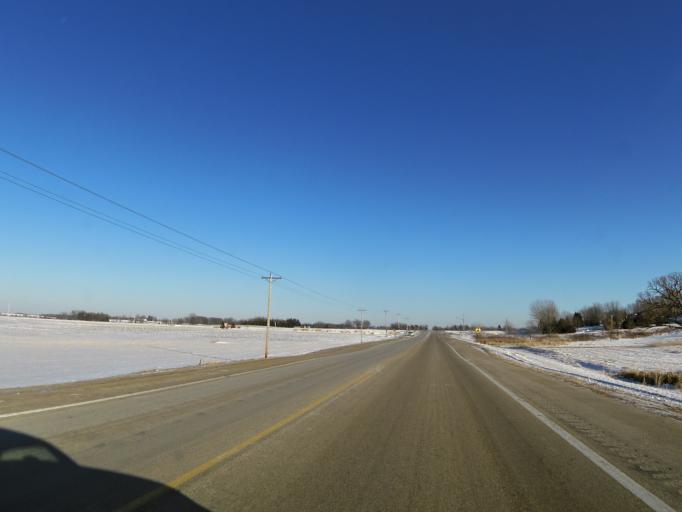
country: US
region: Minnesota
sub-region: Rice County
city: Lonsdale
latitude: 44.4863
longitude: -93.4458
